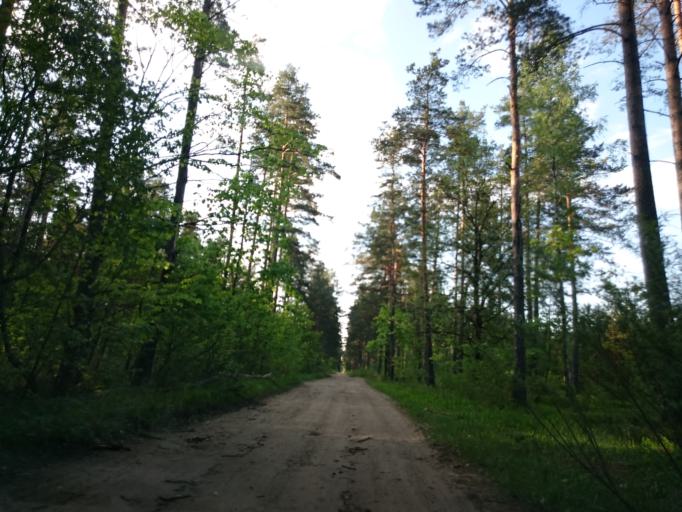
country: LV
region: Stopini
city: Ulbroka
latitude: 56.9476
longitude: 24.2886
